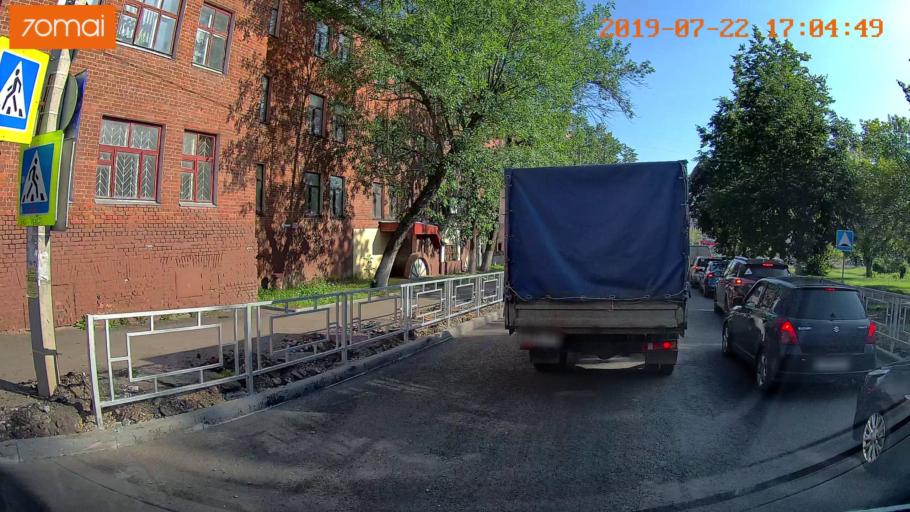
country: RU
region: Ivanovo
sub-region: Gorod Ivanovo
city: Ivanovo
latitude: 56.9954
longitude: 40.9880
